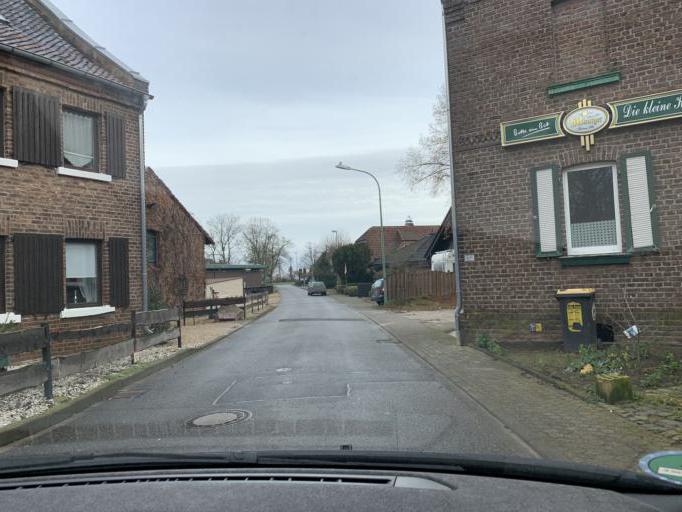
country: DE
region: North Rhine-Westphalia
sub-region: Regierungsbezirk Koln
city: Kerpen
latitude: 50.8173
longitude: 6.7013
